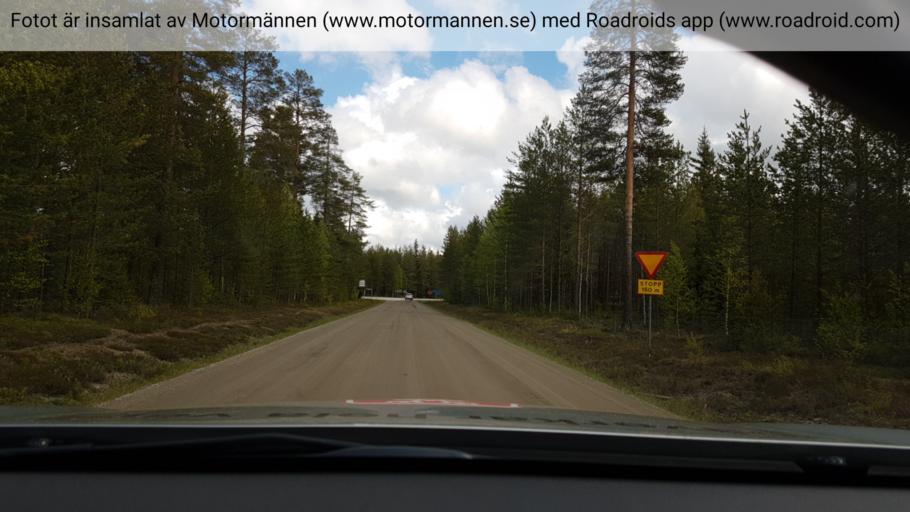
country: SE
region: Vaesterbotten
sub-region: Vindelns Kommun
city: Vindeln
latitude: 64.0832
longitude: 19.6239
